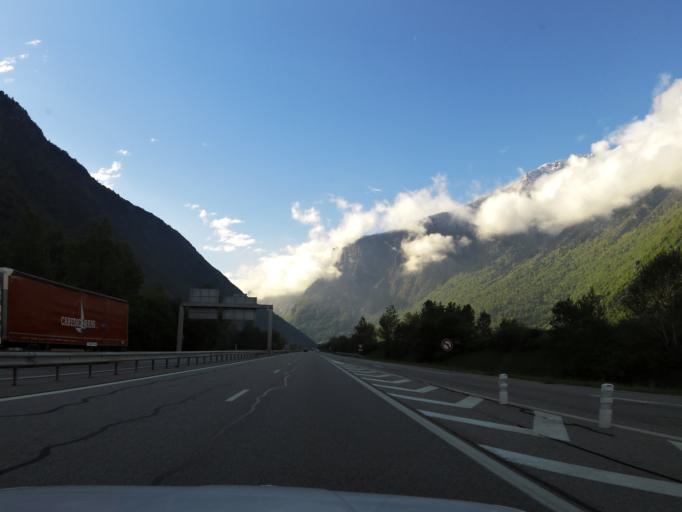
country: FR
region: Rhone-Alpes
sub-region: Departement de la Savoie
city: La Chambre
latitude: 45.3379
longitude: 6.3108
